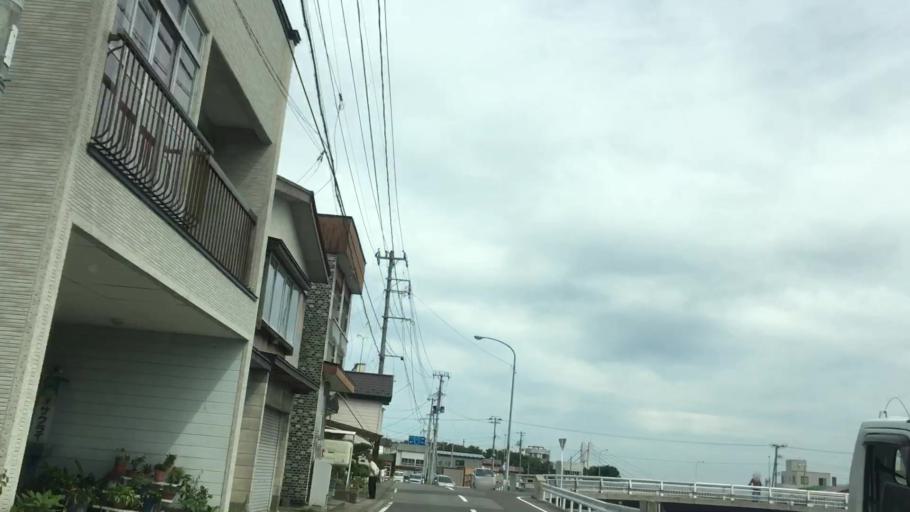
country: JP
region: Aomori
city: Shimokizukuri
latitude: 40.7765
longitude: 140.2169
